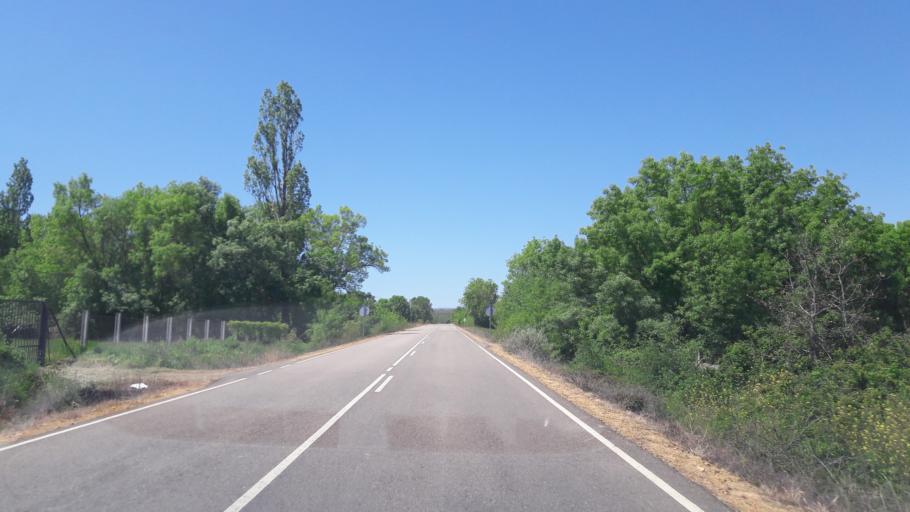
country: ES
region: Castille and Leon
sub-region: Provincia de Salamanca
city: Endrinal
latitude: 40.5907
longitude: -5.8101
